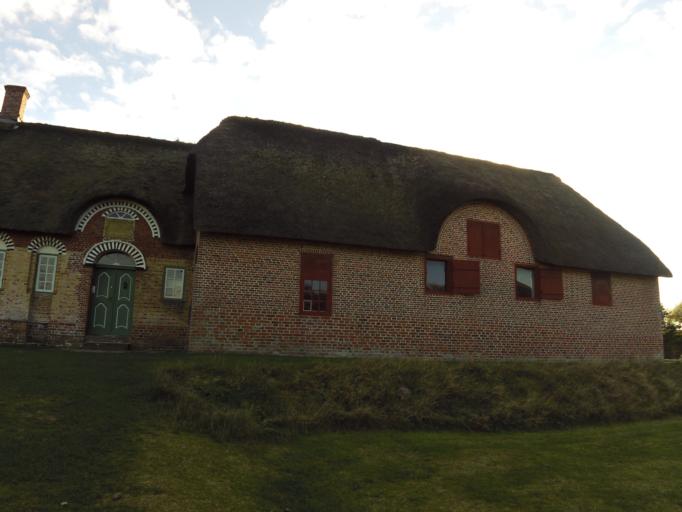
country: DE
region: Schleswig-Holstein
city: List
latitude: 55.1665
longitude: 8.5555
